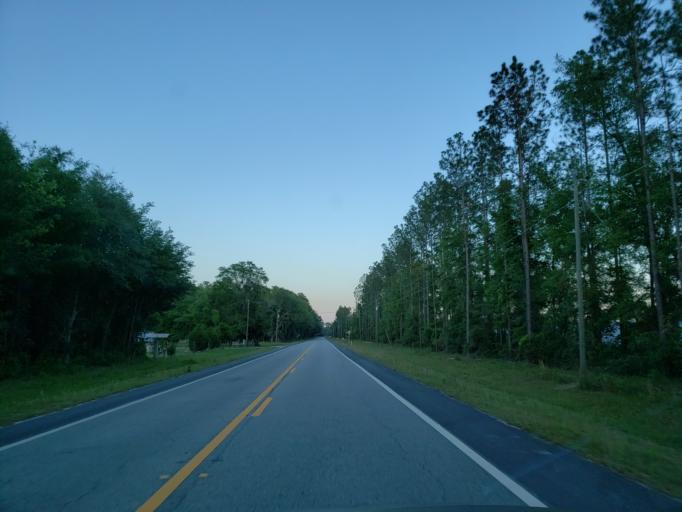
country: US
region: Georgia
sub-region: Echols County
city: Statenville
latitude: 30.5557
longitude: -83.1205
